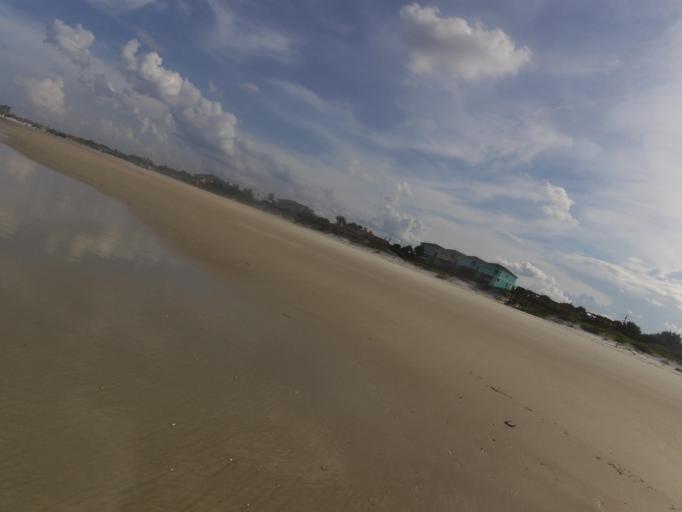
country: US
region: Florida
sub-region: Volusia County
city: Ponce Inlet
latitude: 29.0864
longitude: -80.9252
